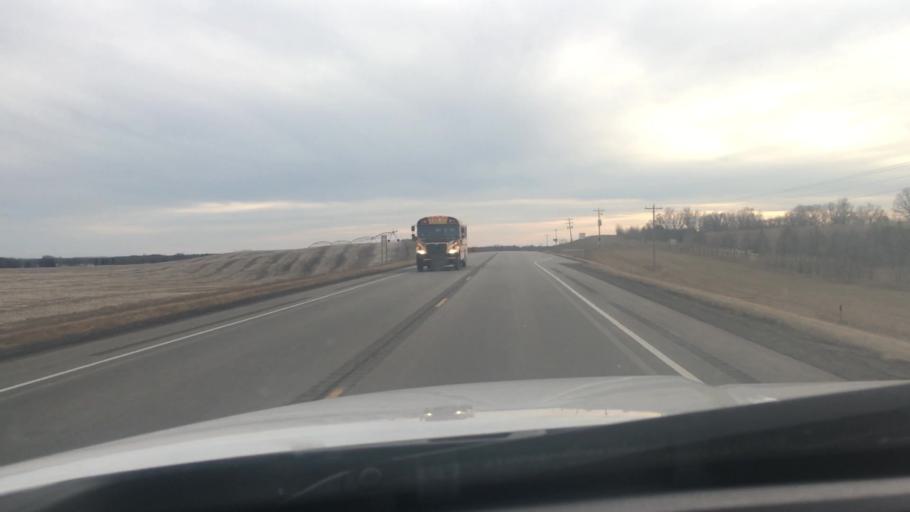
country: US
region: Minnesota
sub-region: Otter Tail County
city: Perham
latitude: 46.3089
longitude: -95.7183
